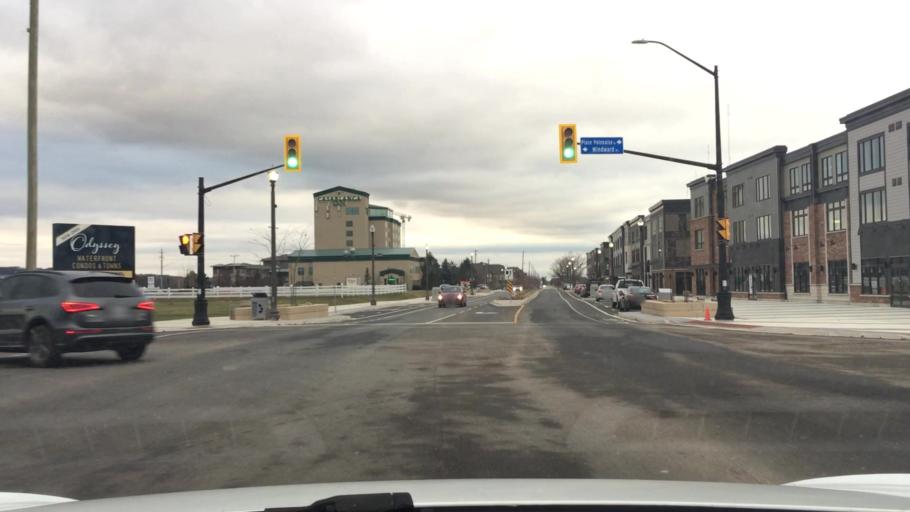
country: CA
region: Ontario
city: Hamilton
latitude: 43.2099
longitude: -79.5983
